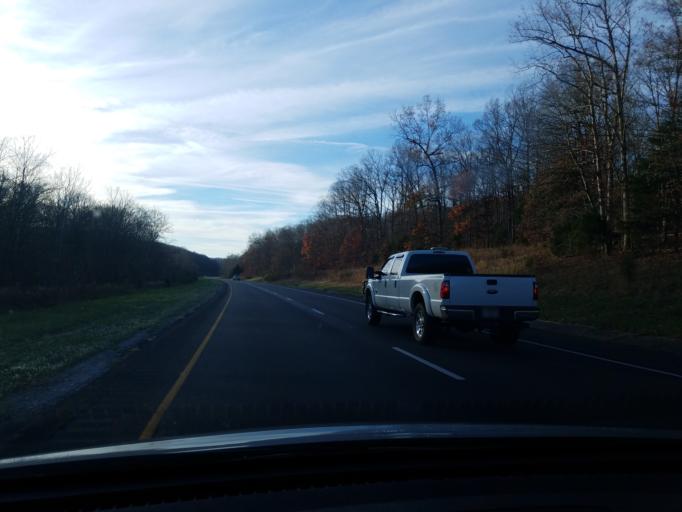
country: US
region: Indiana
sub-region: Crawford County
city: English
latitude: 38.2368
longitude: -86.3810
